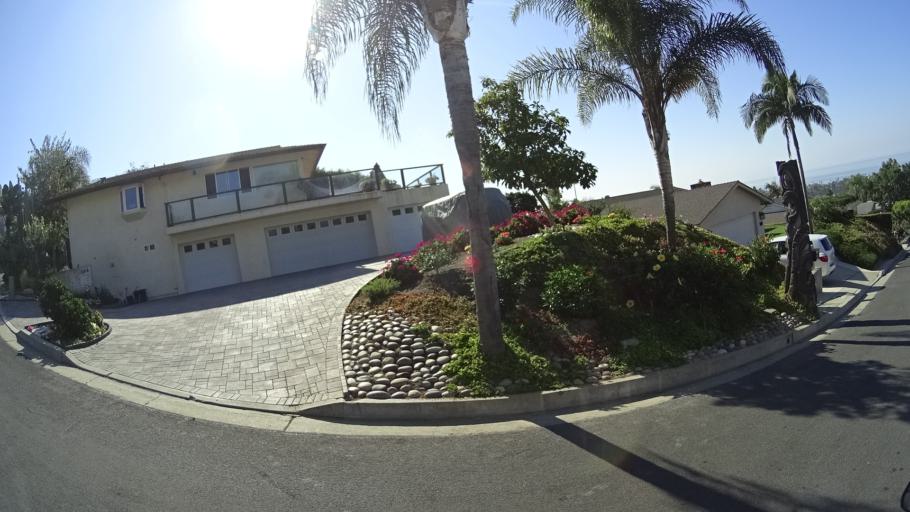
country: US
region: California
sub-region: Orange County
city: San Clemente
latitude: 33.4198
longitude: -117.6002
